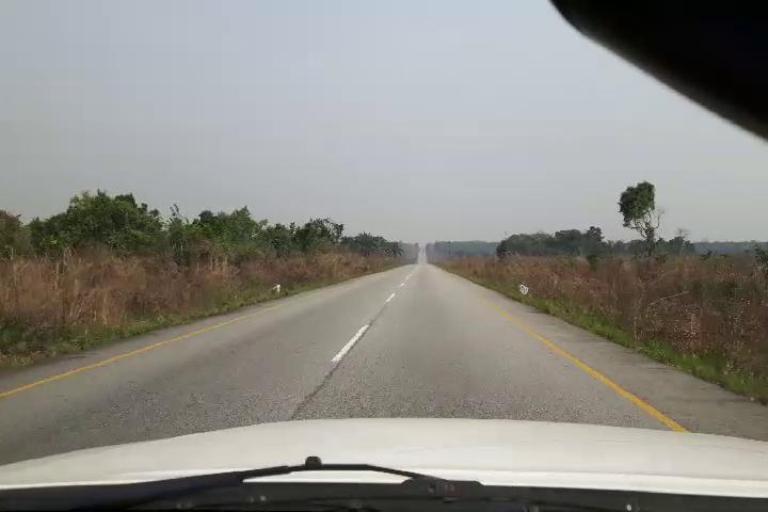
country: SL
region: Southern Province
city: Largo
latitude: 8.2376
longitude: -12.0834
